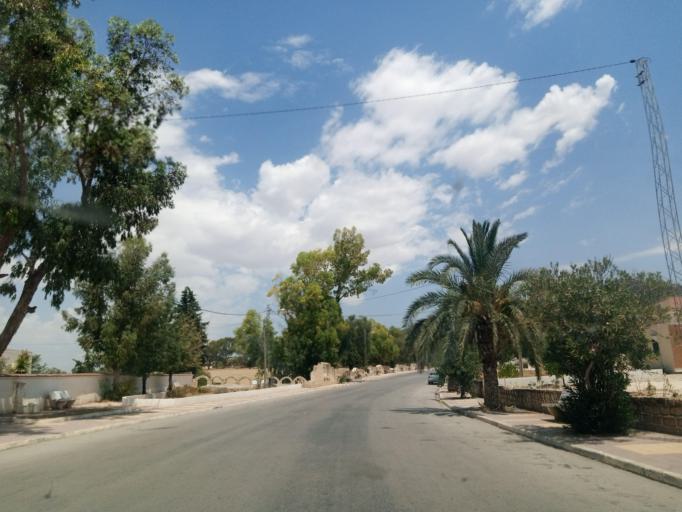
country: TN
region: Kef
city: Nibbar
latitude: 36.3071
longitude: 8.7729
